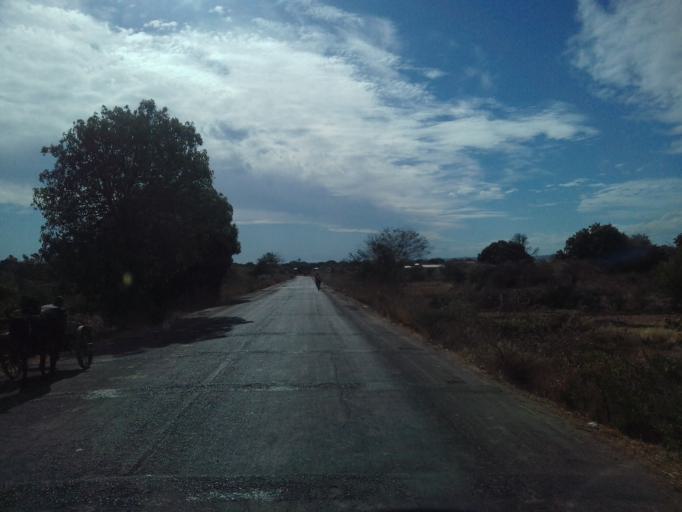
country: MG
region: Sofia
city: Antsohihy
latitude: -15.3409
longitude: 47.8006
